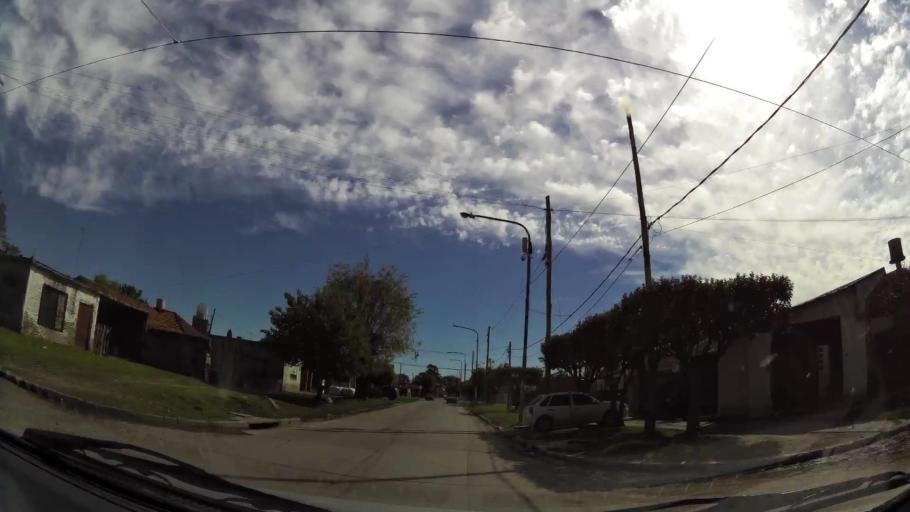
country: AR
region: Buenos Aires
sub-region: Partido de Quilmes
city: Quilmes
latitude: -34.7761
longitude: -58.2956
